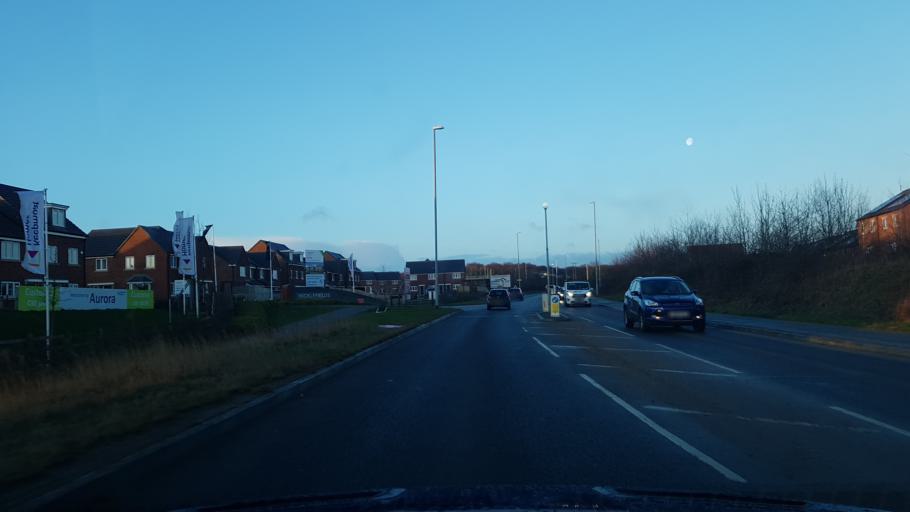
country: GB
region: England
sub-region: City and Borough of Wakefield
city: Castleford
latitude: 53.7093
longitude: -1.3630
